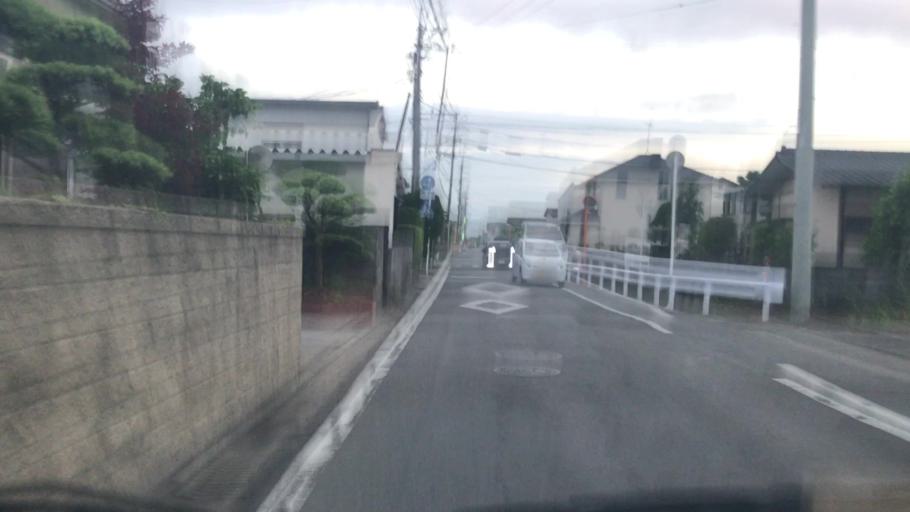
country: JP
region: Saga Prefecture
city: Saga-shi
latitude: 33.2342
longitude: 130.3017
